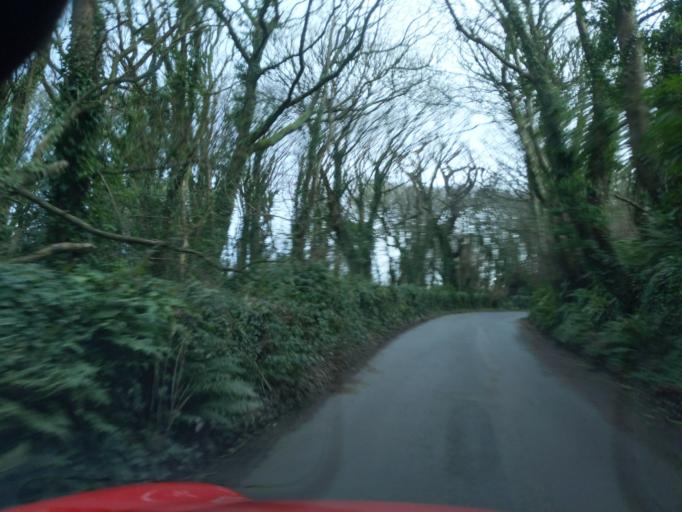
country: GB
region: England
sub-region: Devon
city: Wembury
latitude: 50.3283
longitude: -4.0897
